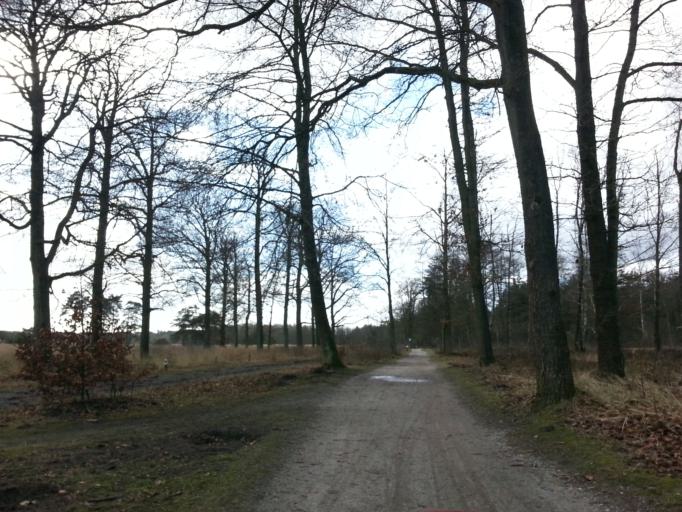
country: NL
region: Utrecht
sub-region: Gemeente Amersfoort
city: Randenbroek
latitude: 52.1285
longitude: 5.3855
